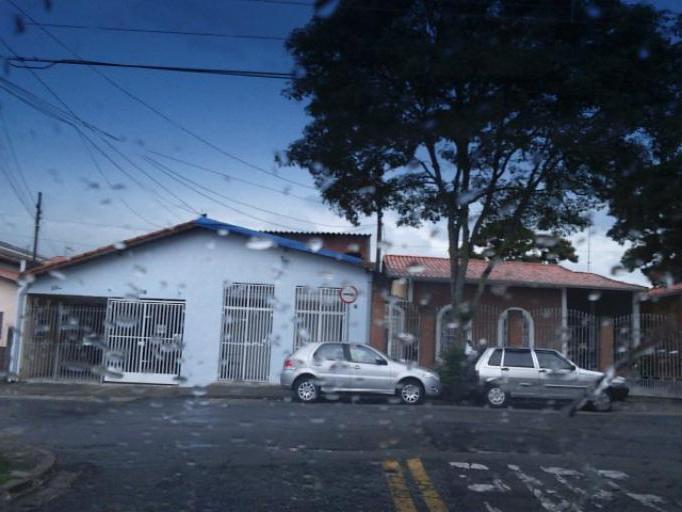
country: BR
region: Sao Paulo
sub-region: Sao Jose Dos Campos
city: Sao Jose dos Campos
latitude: -23.1967
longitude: -45.8783
